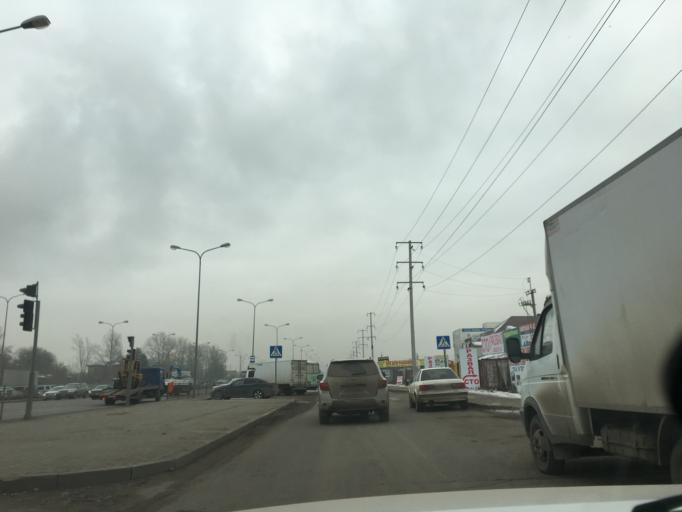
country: KZ
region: Astana Qalasy
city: Astana
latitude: 51.1804
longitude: 71.4631
